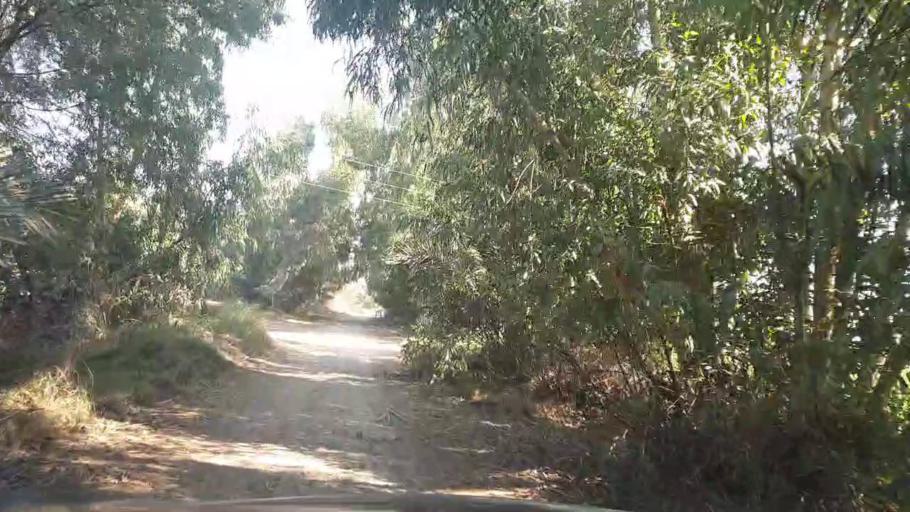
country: PK
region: Sindh
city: Mirpur Mathelo
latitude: 27.9826
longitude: 69.4717
